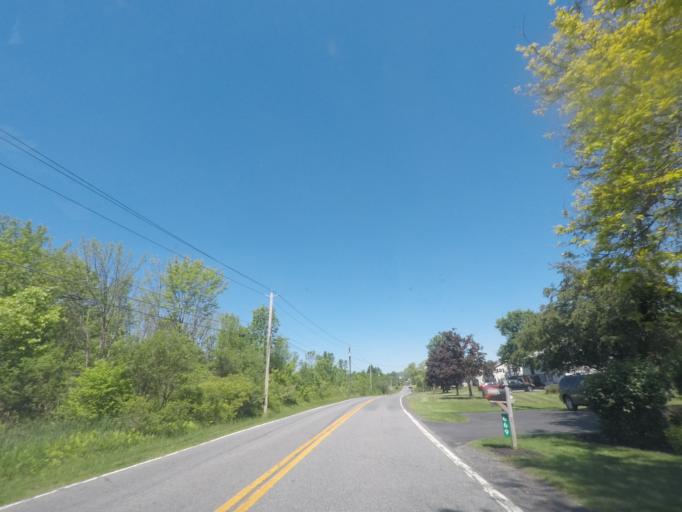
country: US
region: New York
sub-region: Saratoga County
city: Country Knolls
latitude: 42.8750
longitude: -73.8611
